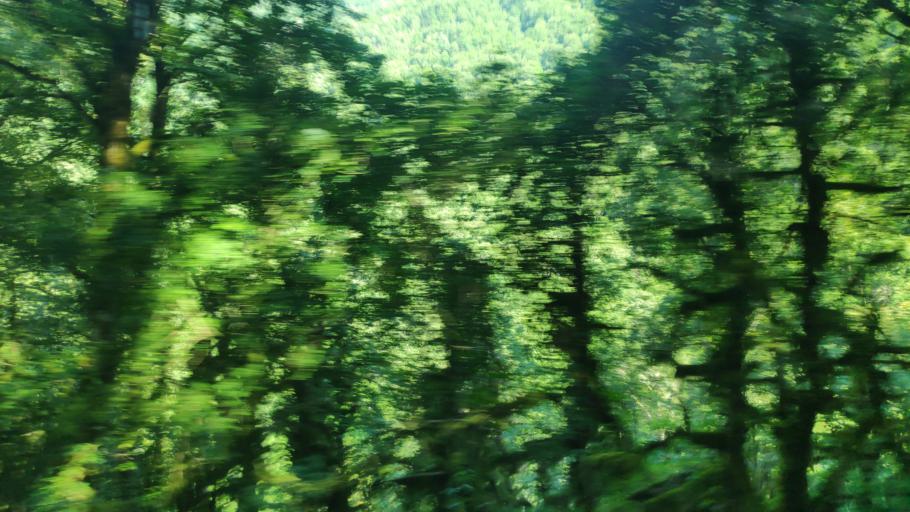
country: GE
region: Abkhazia
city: Gagra
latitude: 43.3536
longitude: 40.4202
